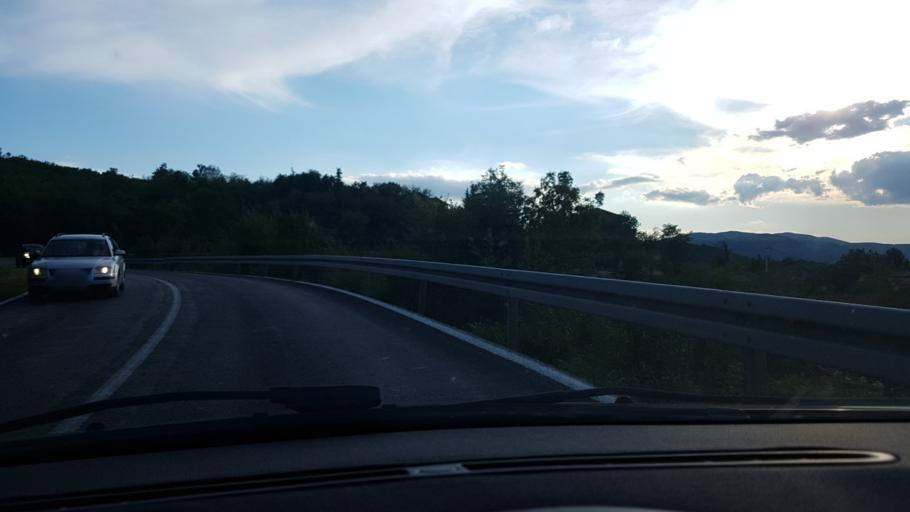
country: HR
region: Splitsko-Dalmatinska
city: Grubine
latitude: 43.4306
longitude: 17.1798
